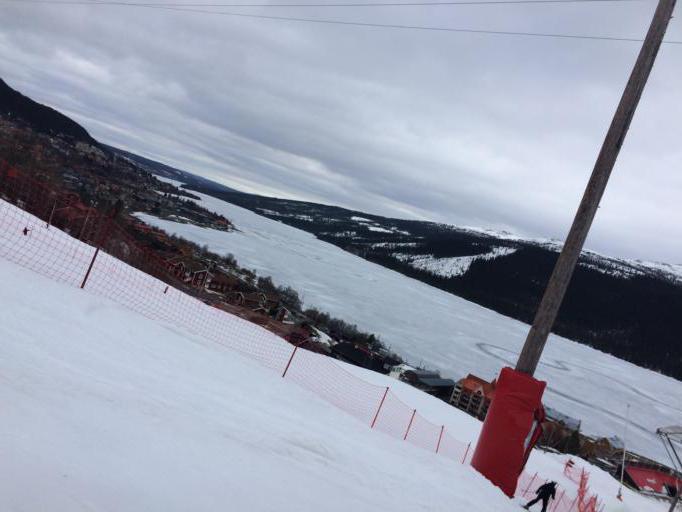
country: SE
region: Jaemtland
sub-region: Are Kommun
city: Are
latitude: 63.4062
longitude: 13.0569
